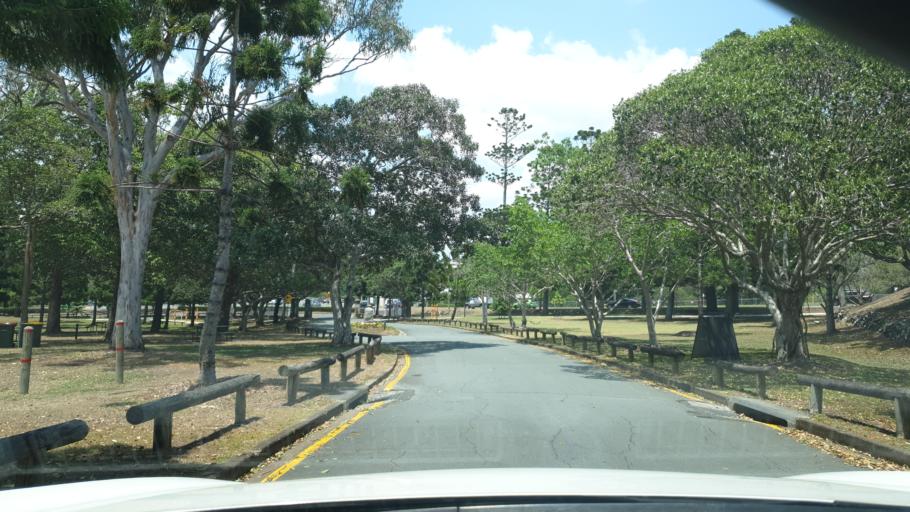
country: AU
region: Queensland
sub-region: Brisbane
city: Chermside West
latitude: -27.3775
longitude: 153.0296
